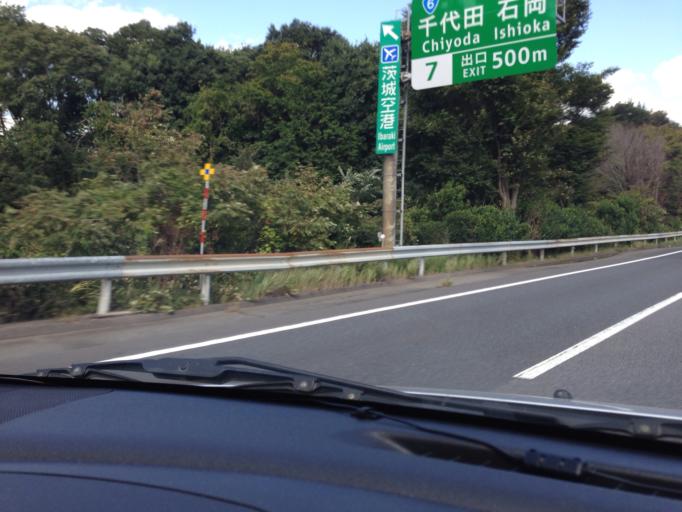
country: JP
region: Ibaraki
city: Ishioka
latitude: 36.1671
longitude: 140.2379
